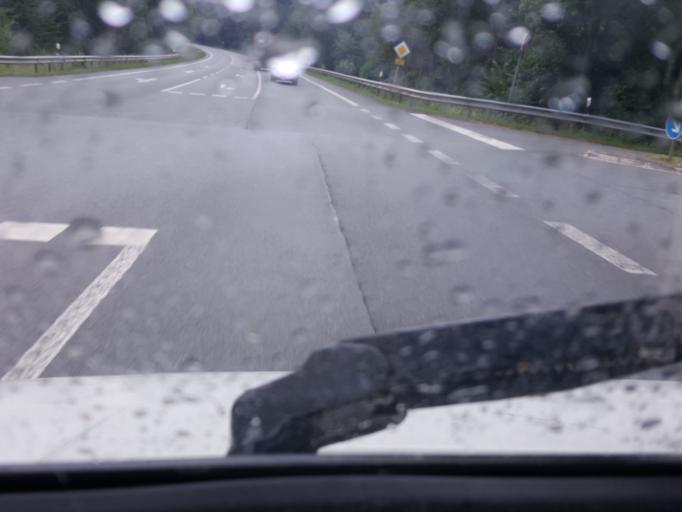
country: DE
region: North Rhine-Westphalia
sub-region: Regierungsbezirk Detmold
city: Petershagen
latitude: 52.3574
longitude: 8.9572
